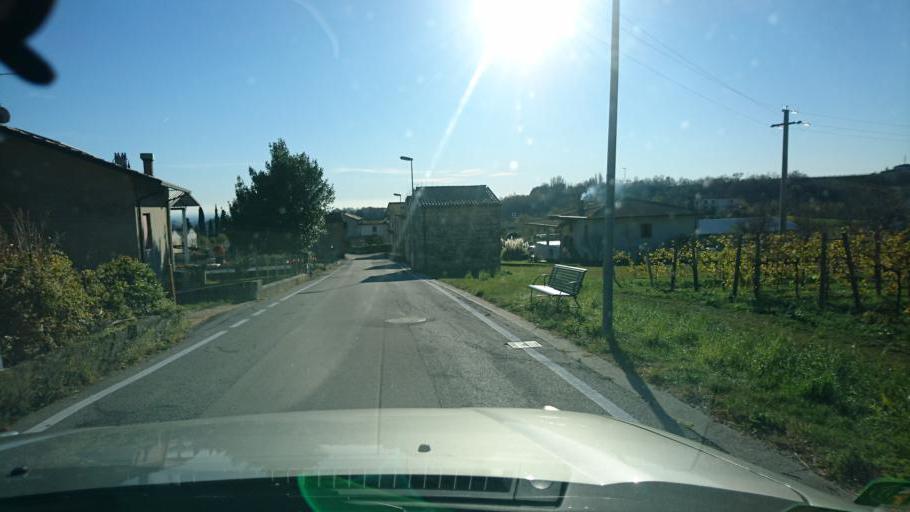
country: IT
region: Veneto
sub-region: Provincia di Treviso
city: Fregona
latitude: 46.0040
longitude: 12.3384
